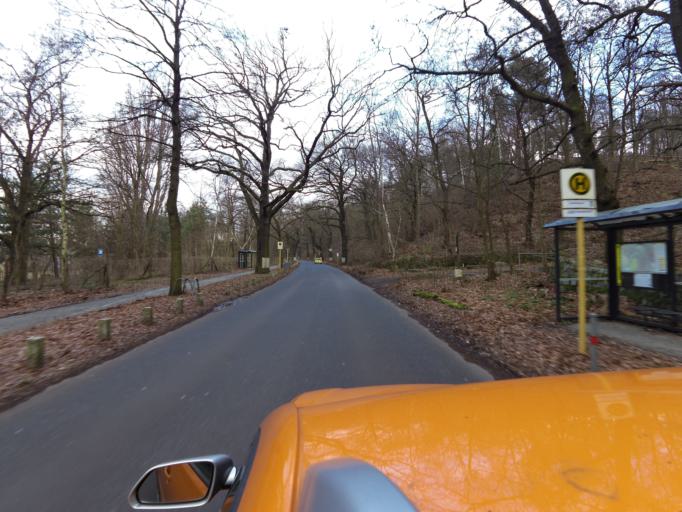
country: DE
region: Berlin
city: Gatow
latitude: 52.4584
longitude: 13.1901
